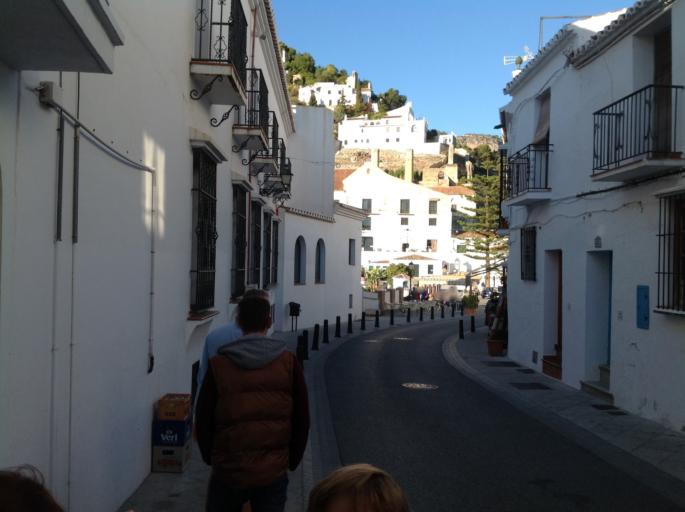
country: ES
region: Andalusia
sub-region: Provincia de Malaga
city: Frigiliana
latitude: 36.7901
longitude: -3.8948
